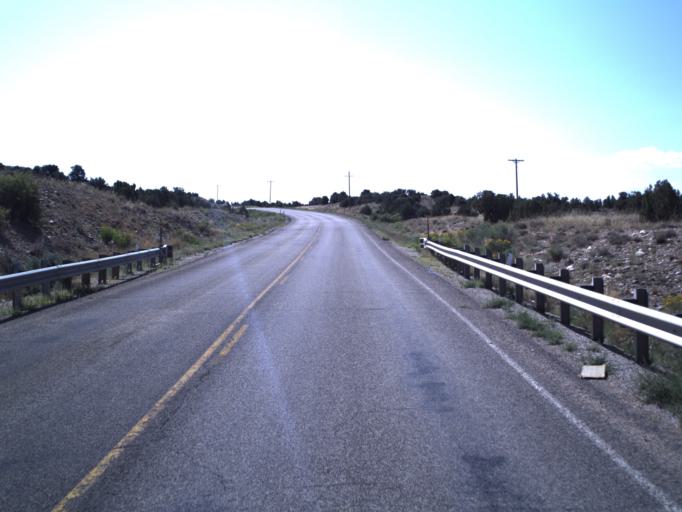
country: US
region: Utah
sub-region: Duchesne County
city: Duchesne
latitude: 40.2583
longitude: -110.4071
